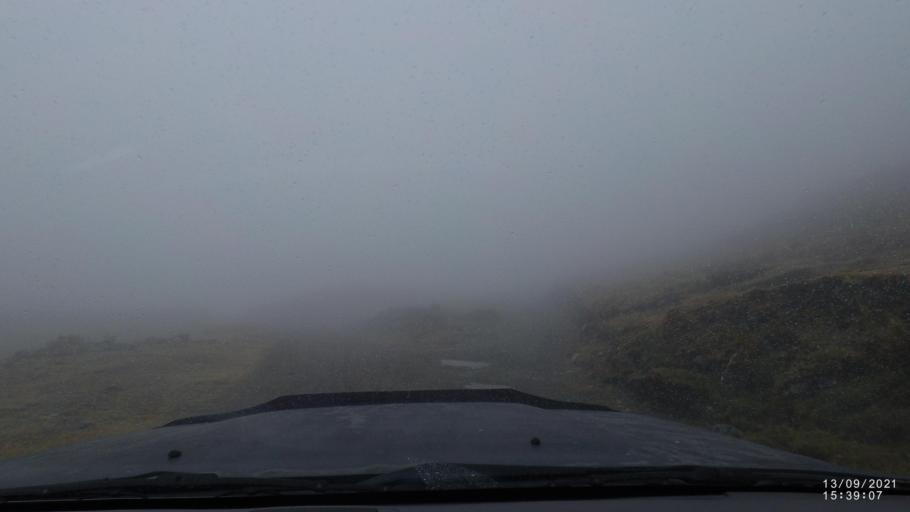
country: BO
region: Cochabamba
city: Colomi
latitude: -17.3263
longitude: -65.7207
